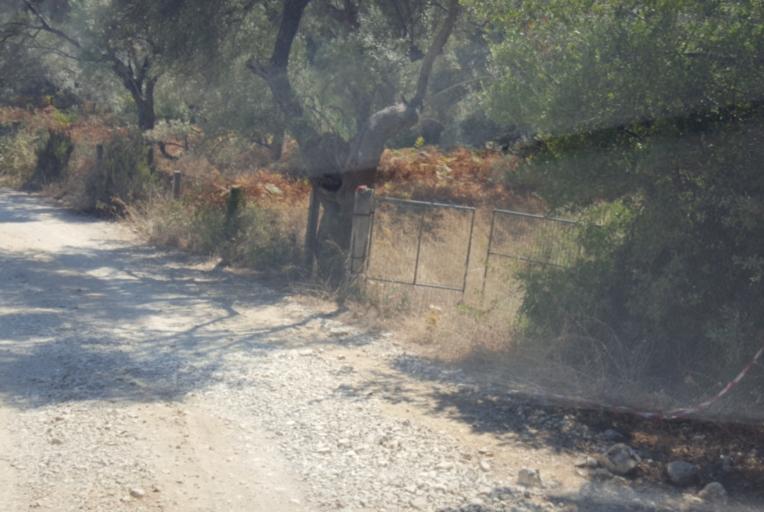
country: GR
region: Ionian Islands
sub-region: Lefkada
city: Nidri
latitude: 38.6561
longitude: 20.7186
